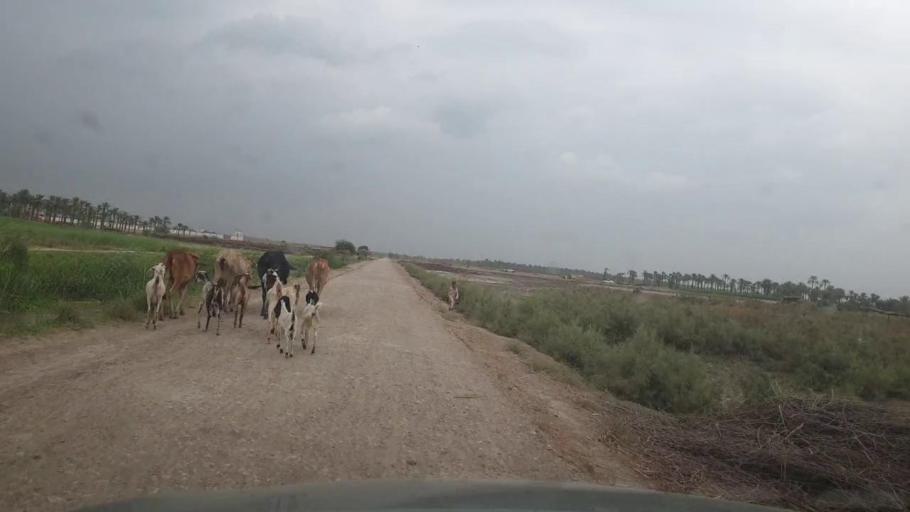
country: PK
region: Sindh
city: Khairpur
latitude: 27.5530
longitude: 68.6925
